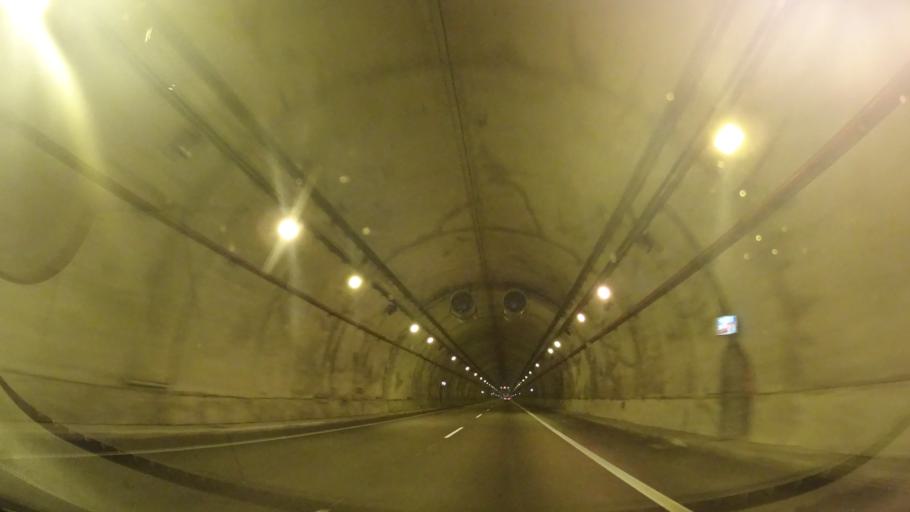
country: ES
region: Asturias
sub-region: Province of Asturias
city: Arriba
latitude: 43.4831
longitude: -5.5283
